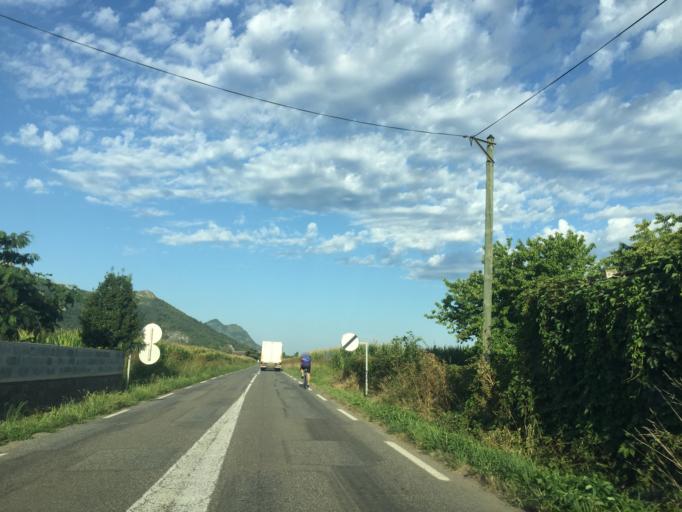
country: FR
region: Midi-Pyrenees
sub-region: Departement des Hautes-Pyrenees
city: Lourdes
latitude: 43.0947
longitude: -0.0008
